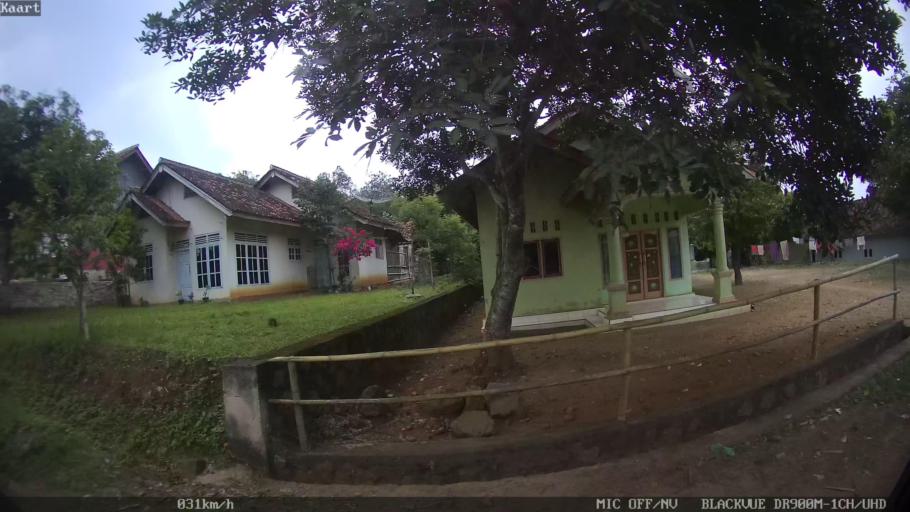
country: ID
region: Lampung
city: Gadingrejo
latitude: -5.3910
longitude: 105.0410
